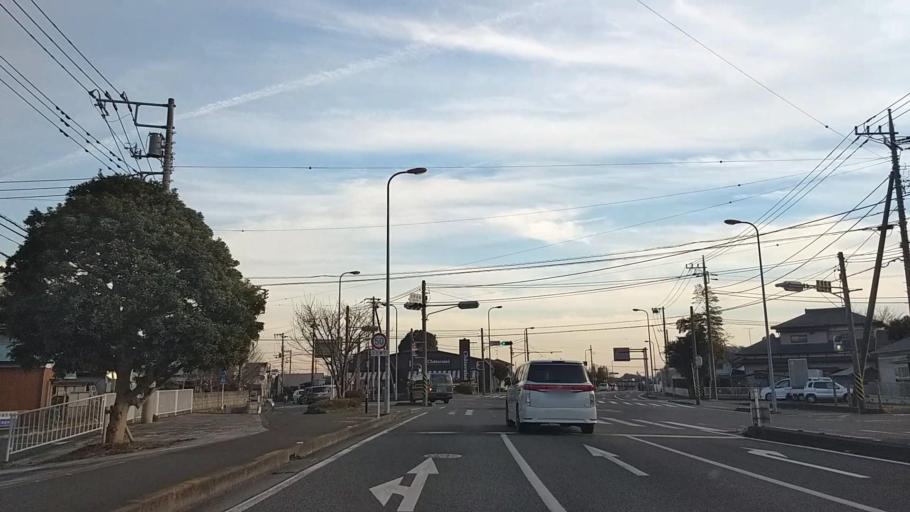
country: JP
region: Kanagawa
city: Atsugi
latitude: 35.4851
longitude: 139.3289
